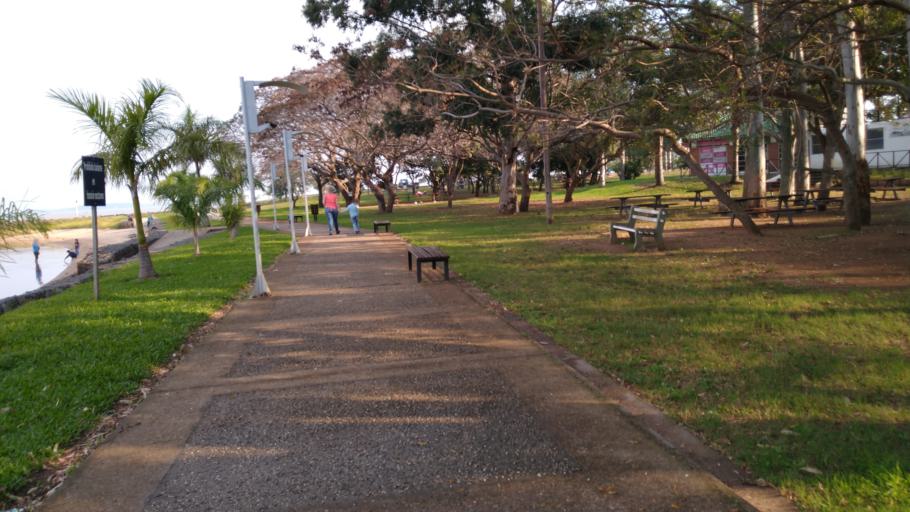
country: AR
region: Entre Rios
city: Santa Ana
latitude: -30.9131
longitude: -57.9251
